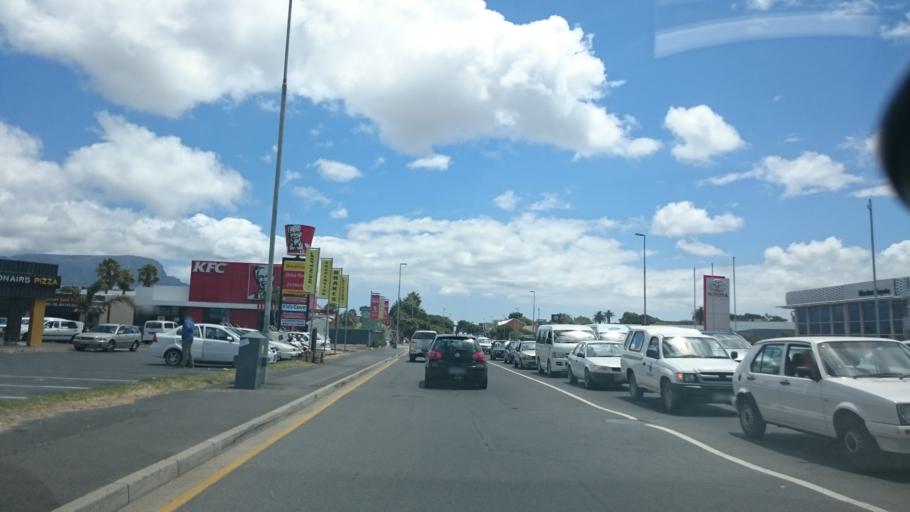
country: ZA
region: Western Cape
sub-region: City of Cape Town
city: Bergvliet
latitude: -34.0657
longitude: 18.4588
